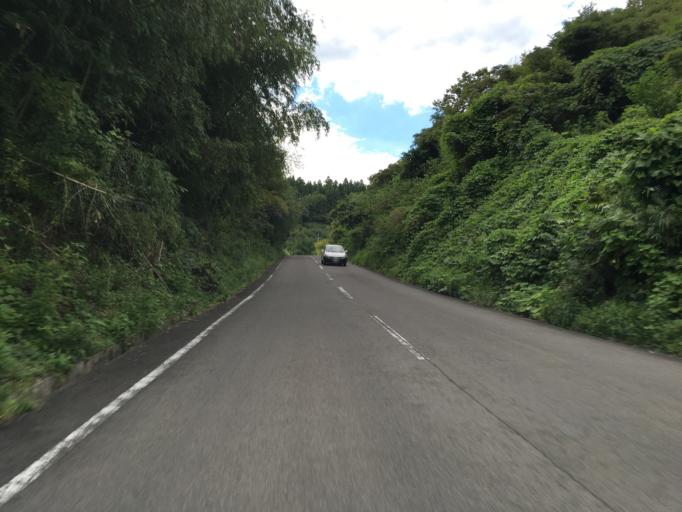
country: JP
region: Fukushima
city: Nihommatsu
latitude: 37.5937
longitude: 140.4974
